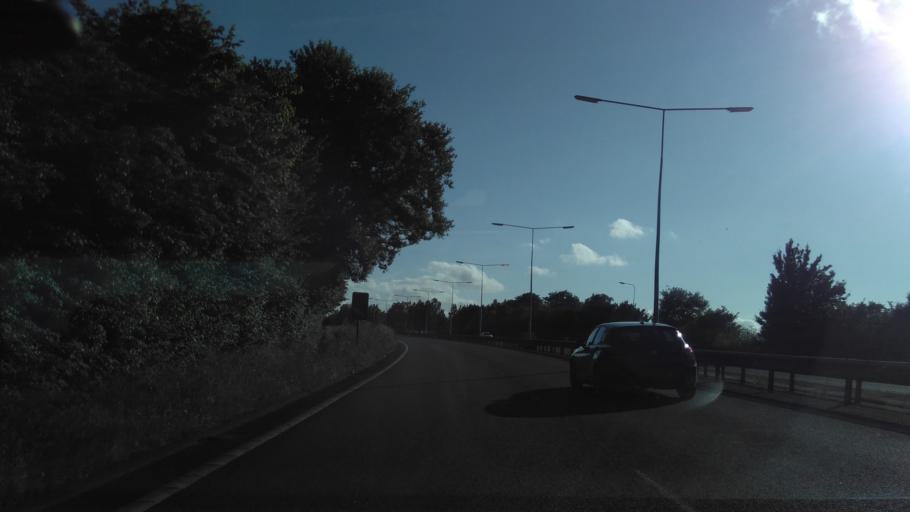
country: GB
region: England
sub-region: Kent
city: Dunkirk
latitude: 51.3110
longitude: 0.9381
